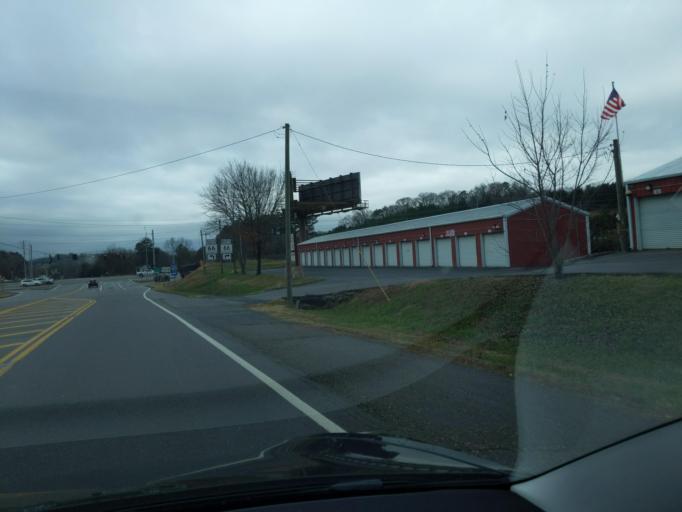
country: US
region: Tennessee
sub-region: Sevier County
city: Sevierville
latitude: 35.9584
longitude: -83.5920
